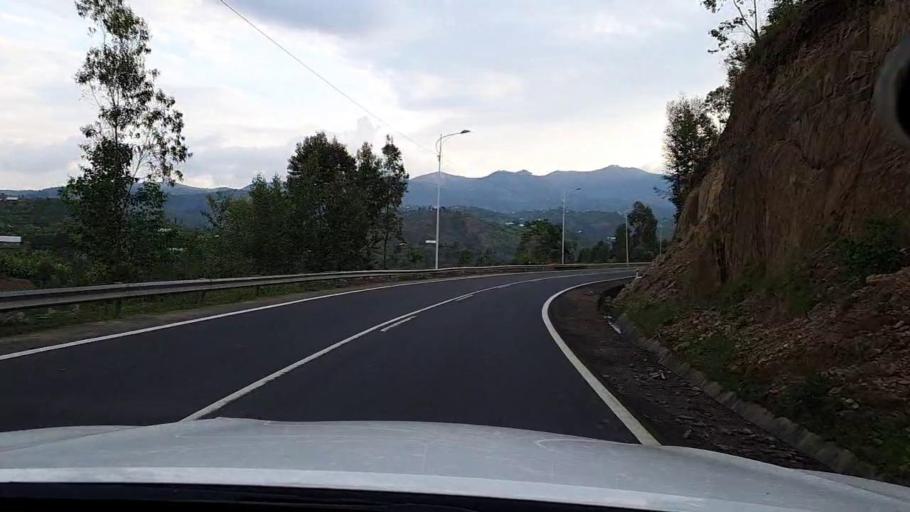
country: RW
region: Western Province
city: Kibuye
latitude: -2.0863
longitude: 29.4060
